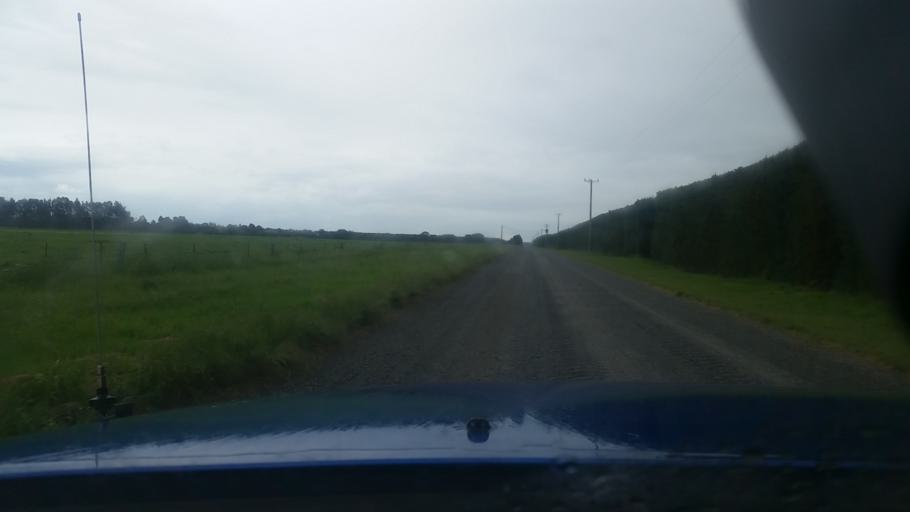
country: NZ
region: Canterbury
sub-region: Ashburton District
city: Rakaia
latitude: -43.9239
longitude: 172.0266
